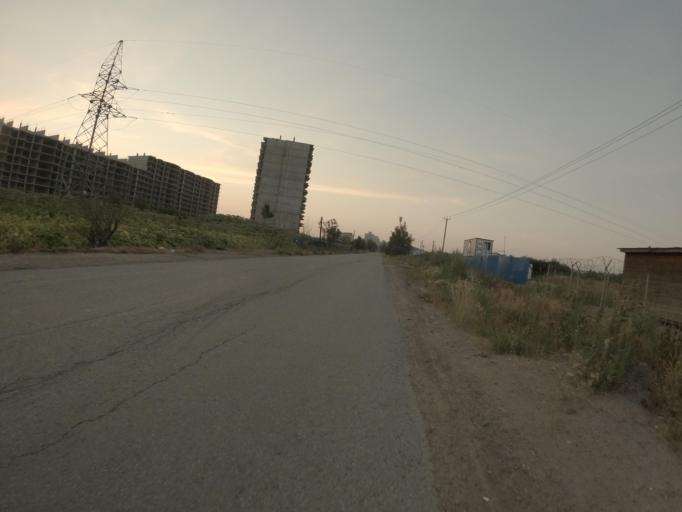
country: RU
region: Leningrad
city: Yanino Vtoroye
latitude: 59.9419
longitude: 30.5531
